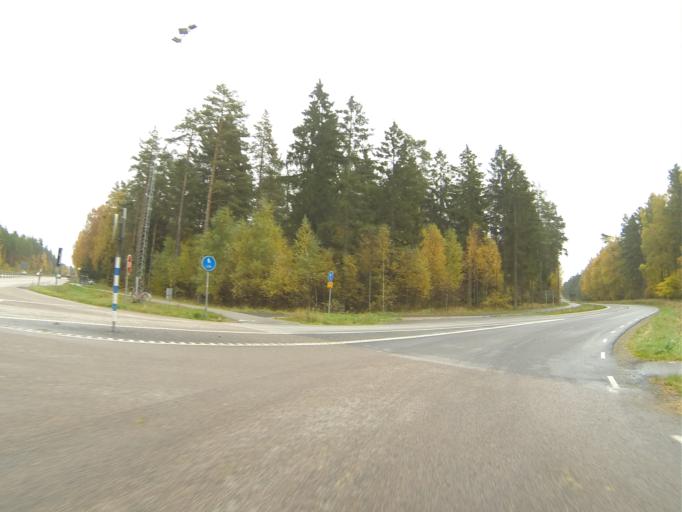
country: SE
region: Skane
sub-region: Sjobo Kommun
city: Sjoebo
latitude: 55.6373
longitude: 13.6545
